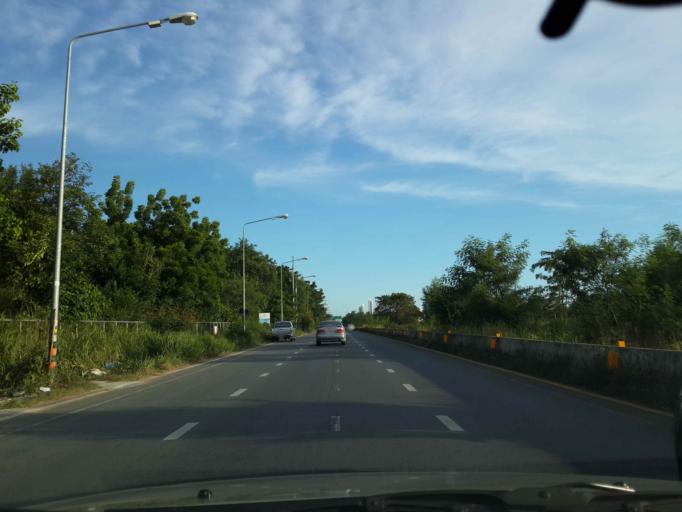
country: TH
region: Chon Buri
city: Phatthaya
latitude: 12.9054
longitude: 100.9012
